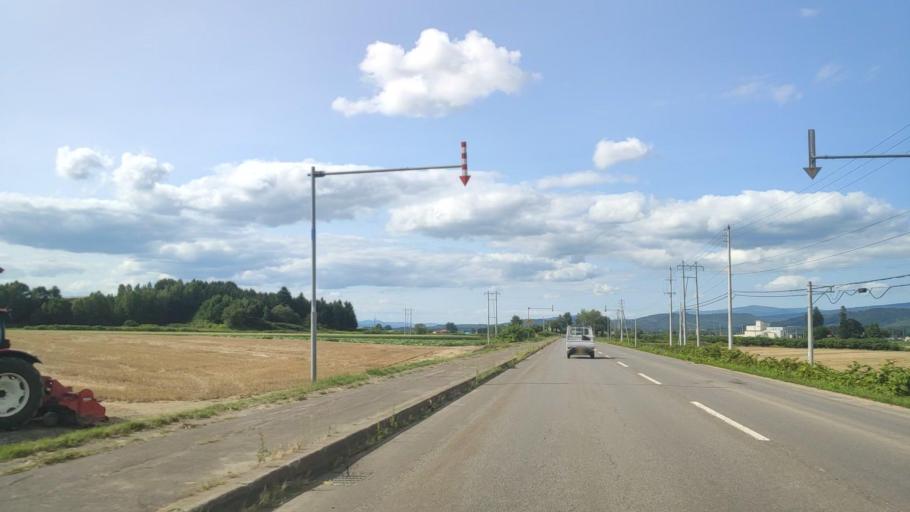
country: JP
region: Hokkaido
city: Nayoro
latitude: 44.4248
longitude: 142.4005
